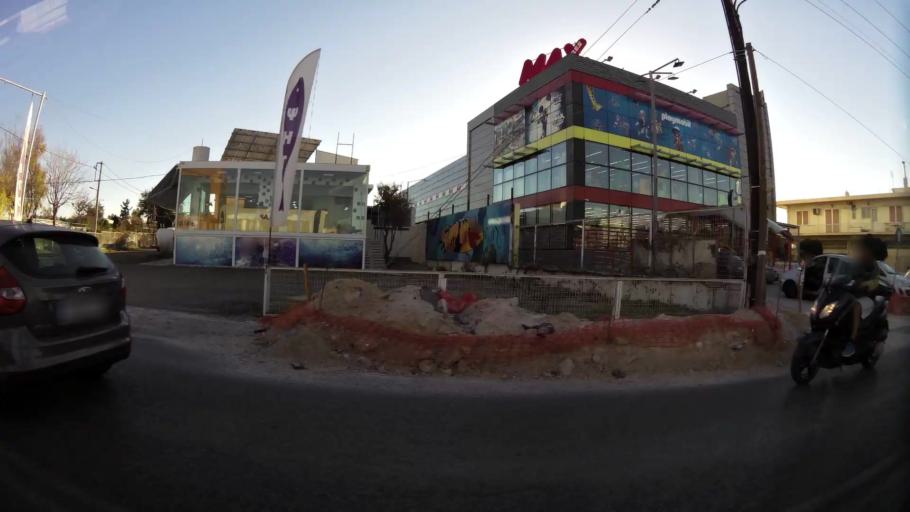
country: GR
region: Attica
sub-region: Nomarchia Athinas
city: Lykovrysi
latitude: 38.0610
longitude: 23.7841
